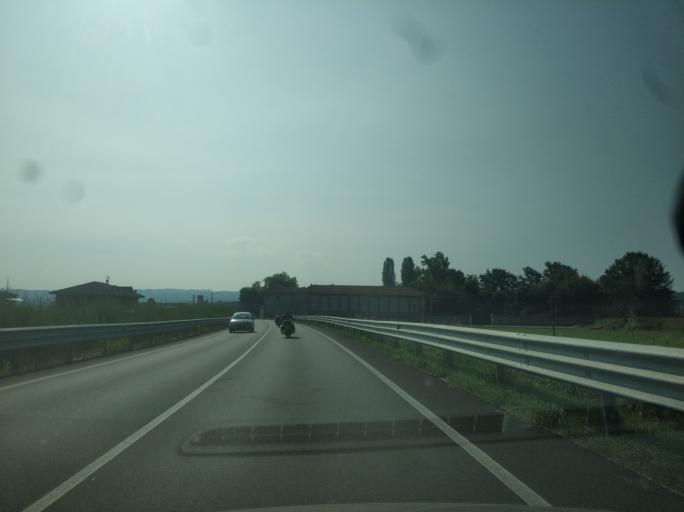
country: IT
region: Piedmont
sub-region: Provincia di Cuneo
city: Roreto
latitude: 44.6679
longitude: 7.8497
